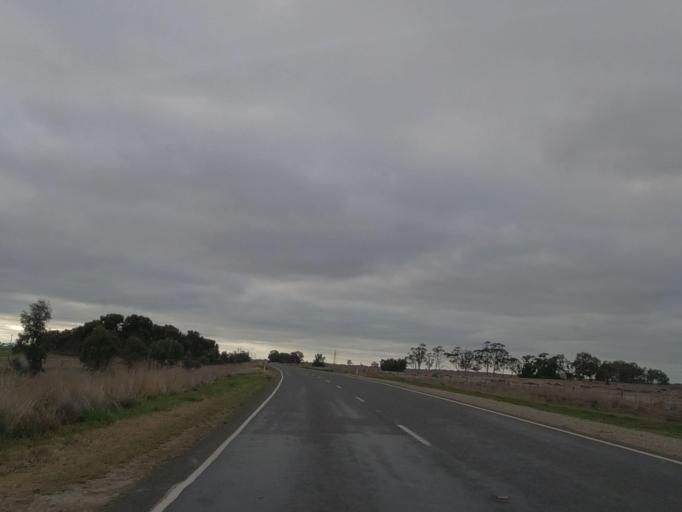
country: AU
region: Victoria
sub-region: Swan Hill
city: Swan Hill
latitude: -35.9193
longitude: 143.9419
